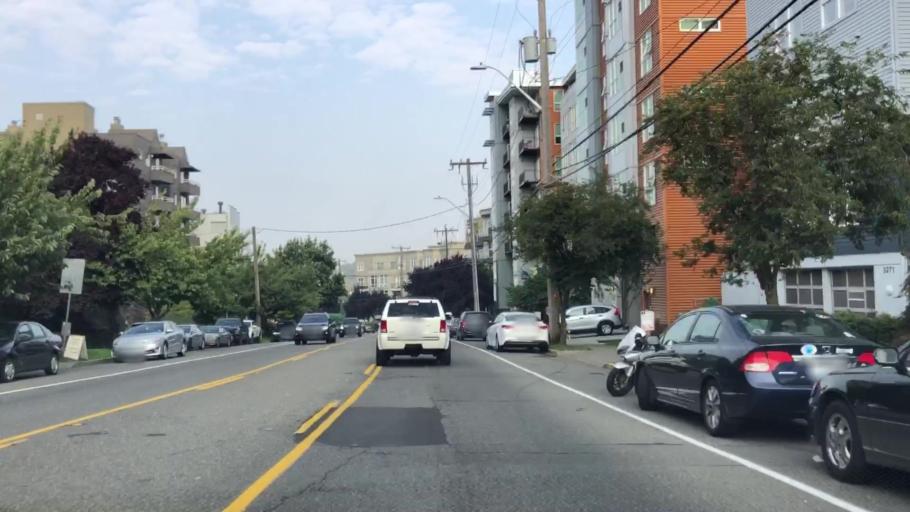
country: US
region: Washington
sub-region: King County
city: White Center
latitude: 47.5641
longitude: -122.3752
